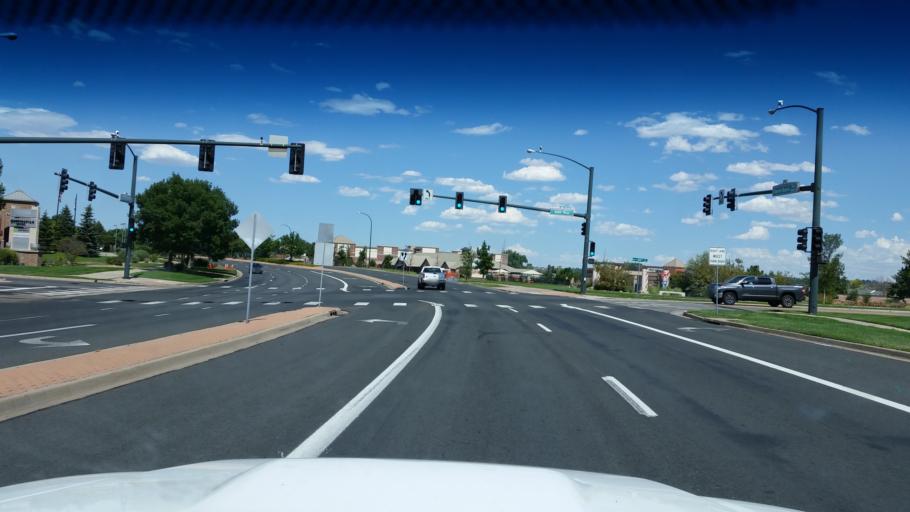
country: US
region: Colorado
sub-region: Broomfield County
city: Broomfield
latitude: 39.8782
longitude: -105.0938
